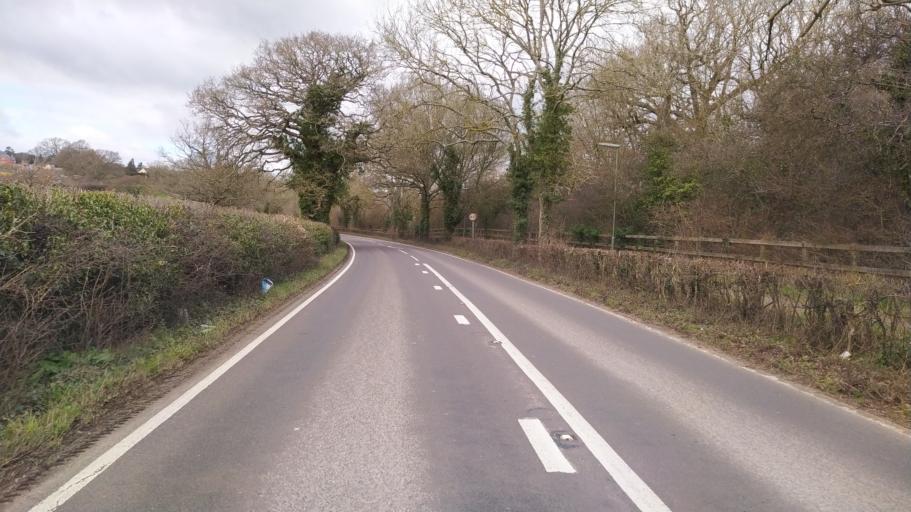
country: GB
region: England
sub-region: Surrey
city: Farnham
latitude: 51.2246
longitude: -0.8038
